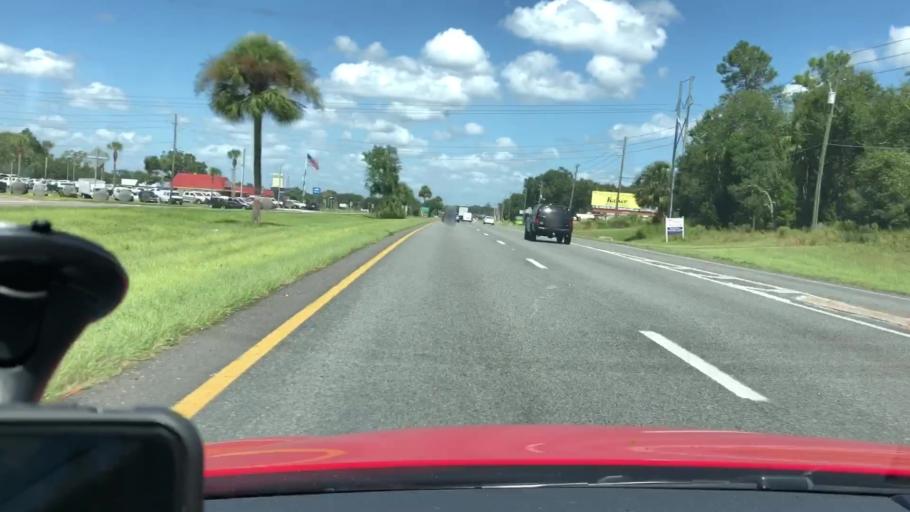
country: US
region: Florida
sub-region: Volusia County
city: Orange City
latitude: 28.9764
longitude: -81.2990
